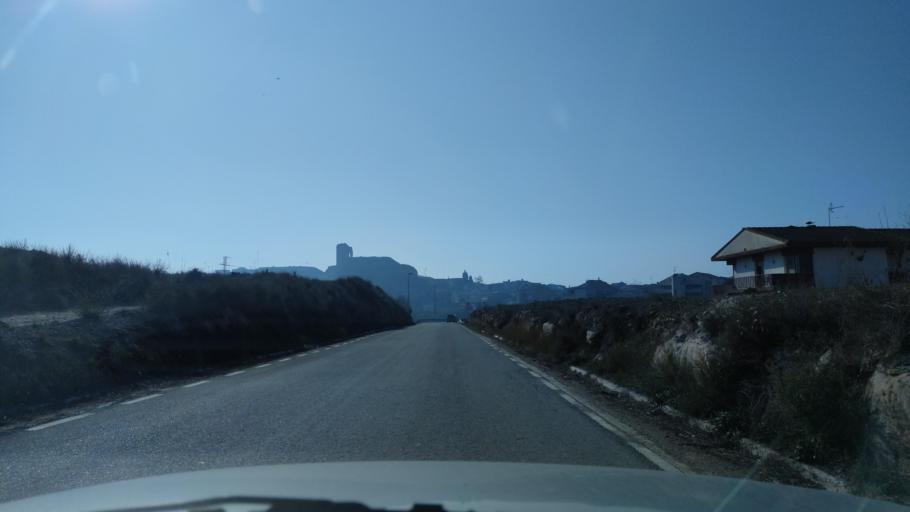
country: ES
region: Catalonia
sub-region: Provincia de Lleida
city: Torrebesses
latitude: 41.4619
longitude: 0.5643
